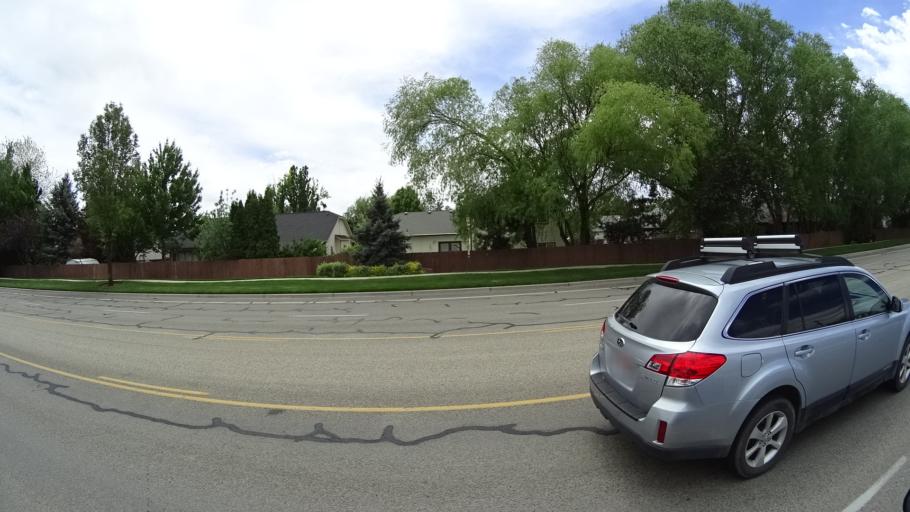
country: US
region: Idaho
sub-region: Ada County
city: Meridian
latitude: 43.5903
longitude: -116.3812
